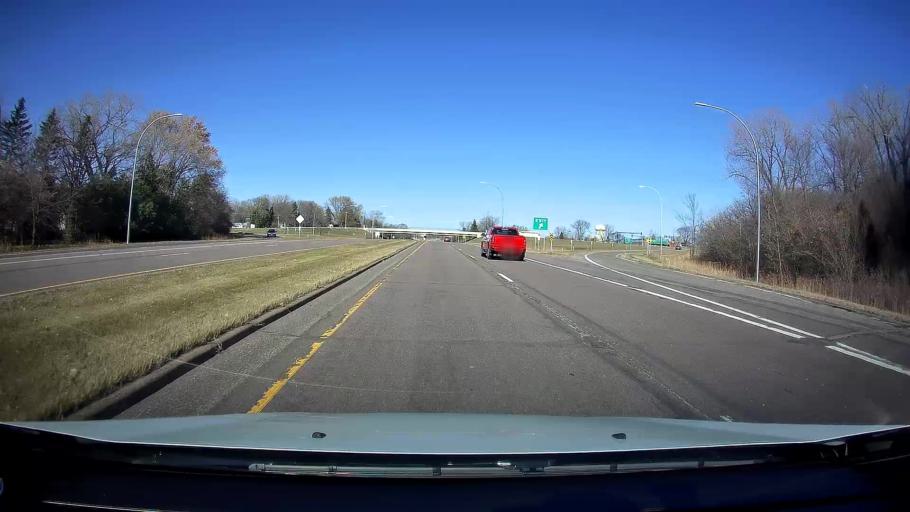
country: US
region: Minnesota
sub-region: Ramsey County
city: Arden Hills
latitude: 45.0486
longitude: -93.1557
